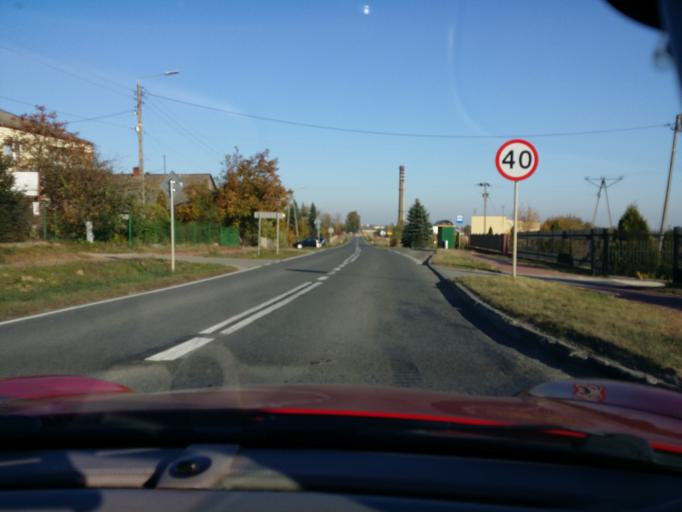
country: PL
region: Masovian Voivodeship
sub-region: Powiat szydlowiecki
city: Mirow
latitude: 51.2444
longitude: 21.0037
